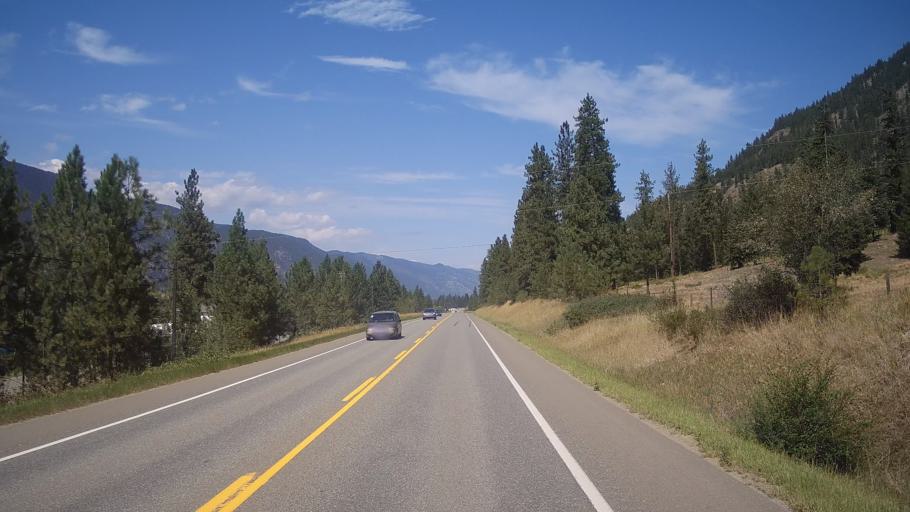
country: CA
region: British Columbia
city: Kamloops
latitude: 50.9468
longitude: -120.2342
